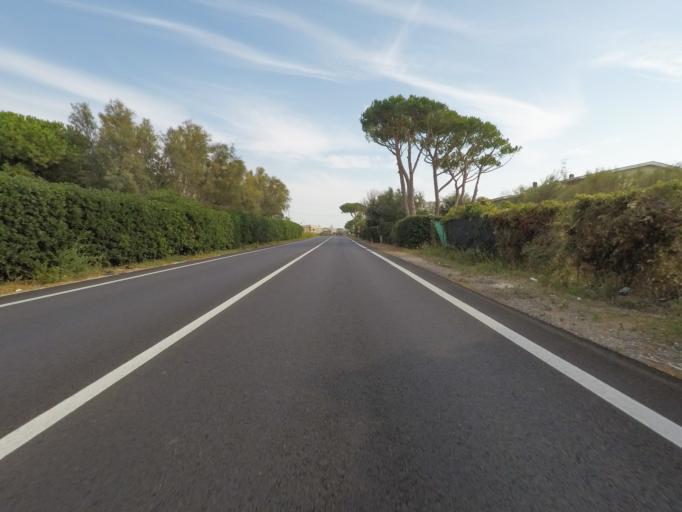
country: IT
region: Latium
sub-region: Citta metropolitana di Roma Capitale
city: Santa Marinella
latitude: 42.0465
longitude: 11.8236
